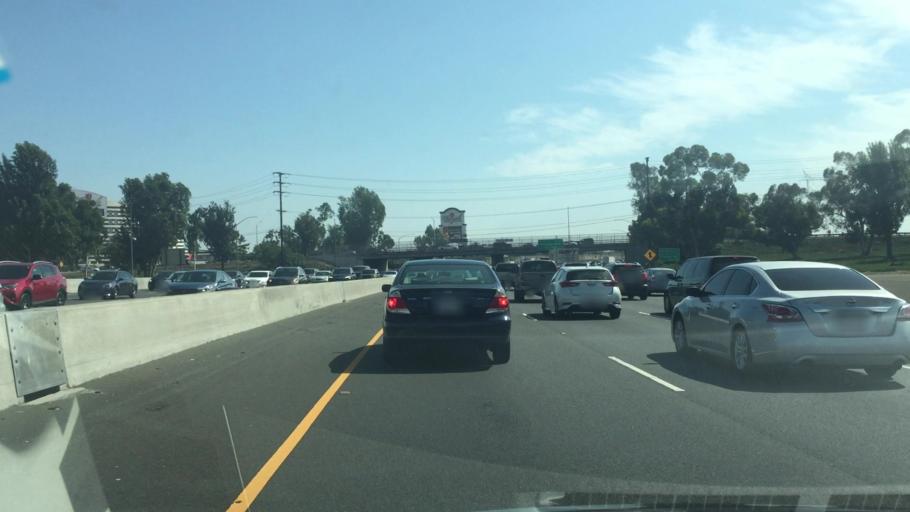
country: US
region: California
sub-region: Los Angeles County
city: Bell Gardens
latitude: 33.9703
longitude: -118.1678
